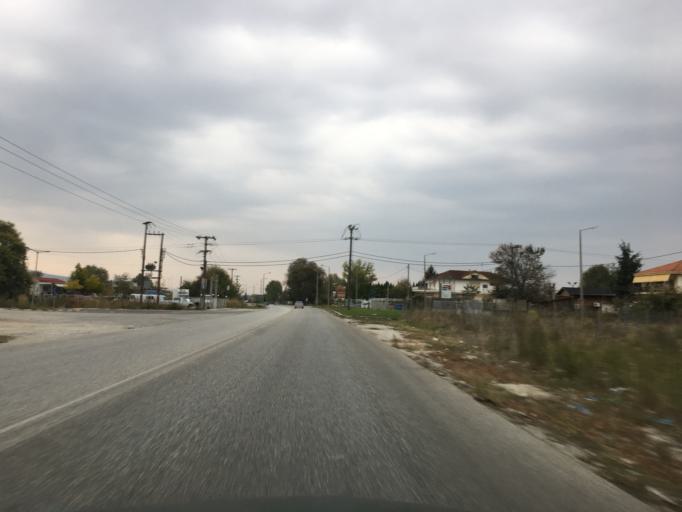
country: GR
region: Thessaly
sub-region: Trikala
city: Trikala
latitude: 39.5558
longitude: 21.7913
